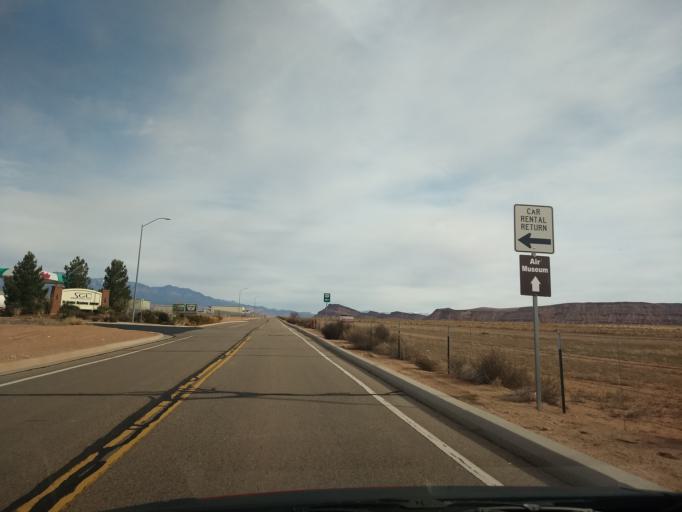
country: US
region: Utah
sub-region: Washington County
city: Washington
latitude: 37.0307
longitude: -113.5052
